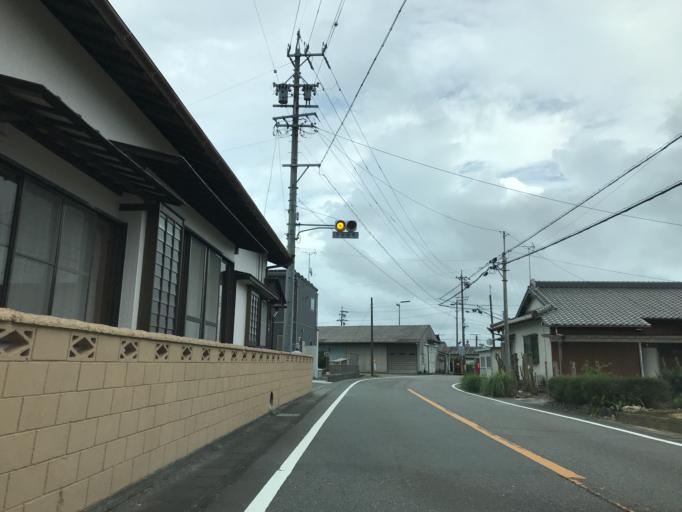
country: JP
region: Shizuoka
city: Sagara
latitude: 34.7046
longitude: 138.1450
